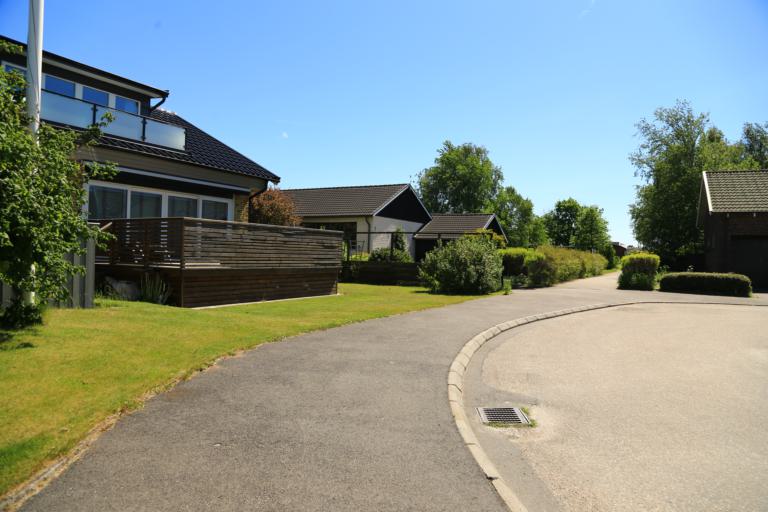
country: SE
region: Halland
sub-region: Varbergs Kommun
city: Varberg
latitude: 57.1091
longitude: 12.2784
